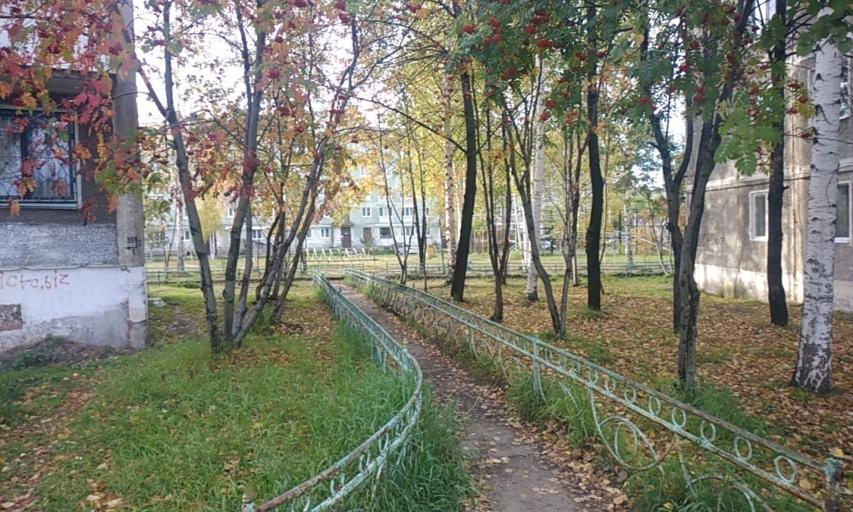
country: RU
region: Sverdlovsk
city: Krasnoural'sk
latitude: 58.3571
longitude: 60.0422
